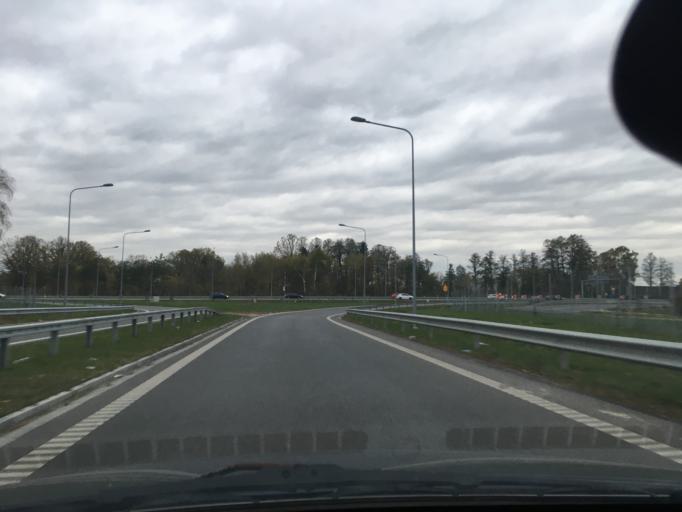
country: PL
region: Lodz Voivodeship
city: Zabia Wola
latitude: 52.0512
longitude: 20.7213
